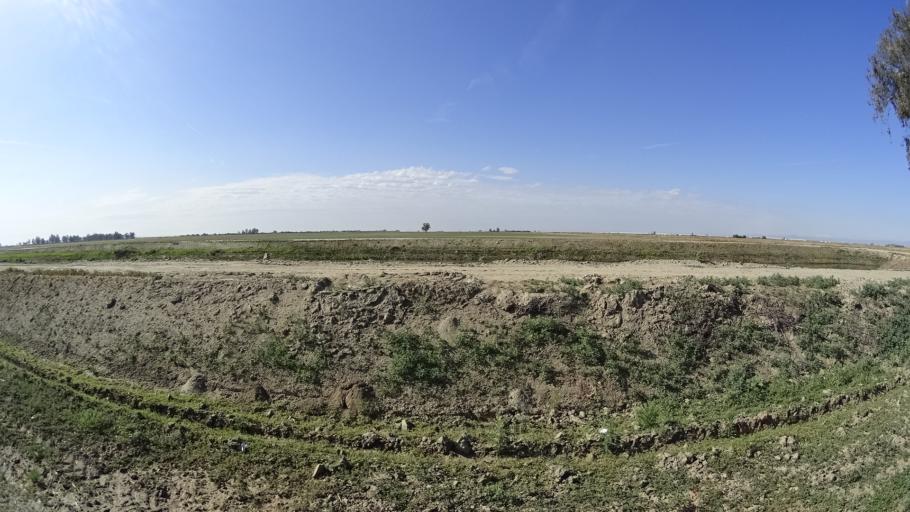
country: US
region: California
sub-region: Kings County
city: Home Garden
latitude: 36.2258
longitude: -119.6720
